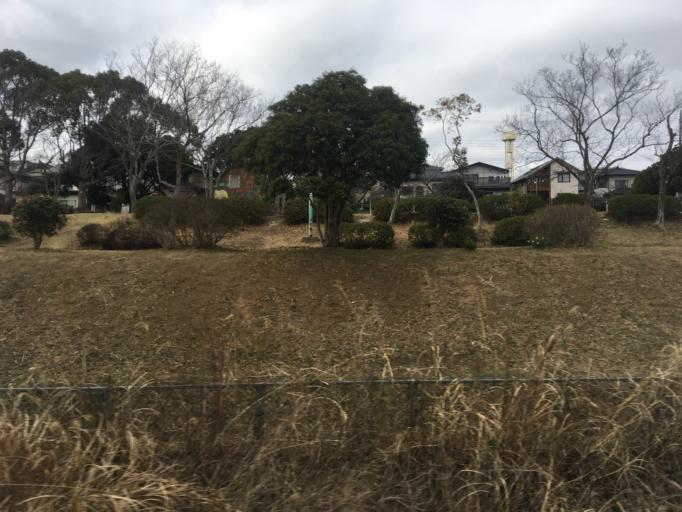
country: JP
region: Chiba
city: Shisui
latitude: 35.7287
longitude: 140.2730
